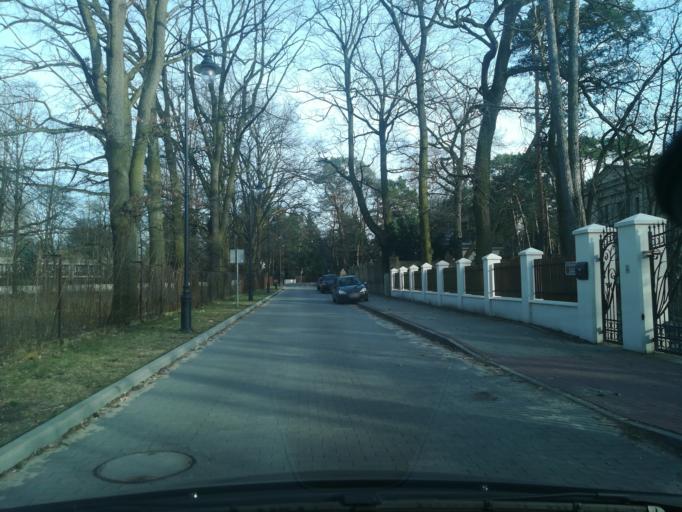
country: PL
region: Masovian Voivodeship
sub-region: Powiat piaseczynski
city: Konstancin-Jeziorna
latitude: 52.0842
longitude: 21.1241
